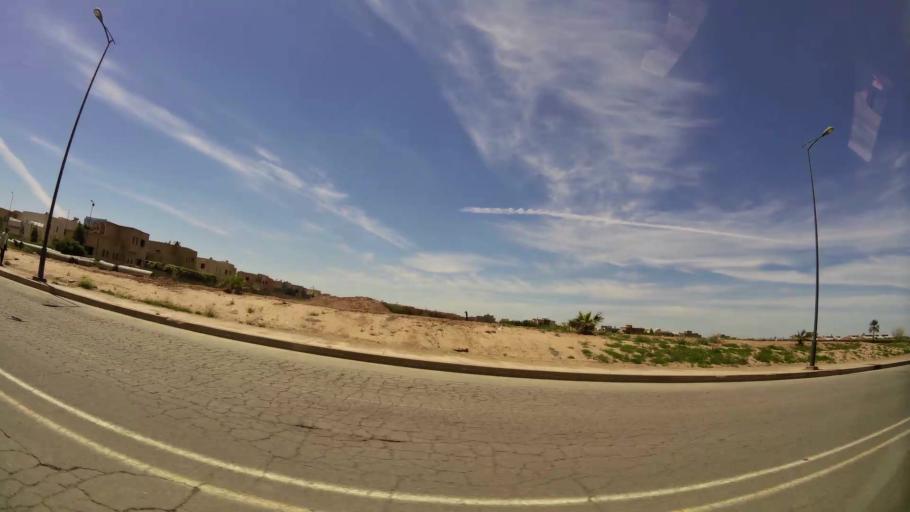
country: MA
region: Marrakech-Tensift-Al Haouz
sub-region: Marrakech
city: Marrakesh
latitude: 31.6497
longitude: -8.0675
